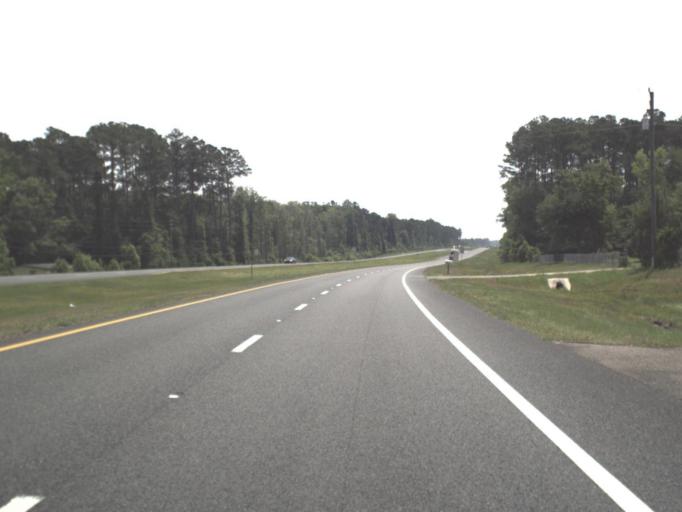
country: US
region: Florida
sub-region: Nassau County
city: Yulee
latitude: 30.6160
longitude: -81.7134
